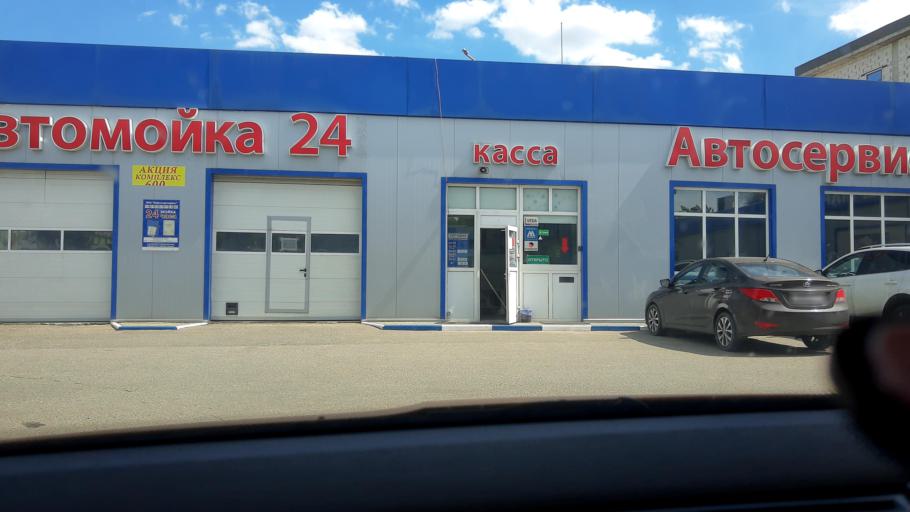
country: RU
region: Moskovskaya
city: Petrovskaya
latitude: 55.5336
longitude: 37.8128
